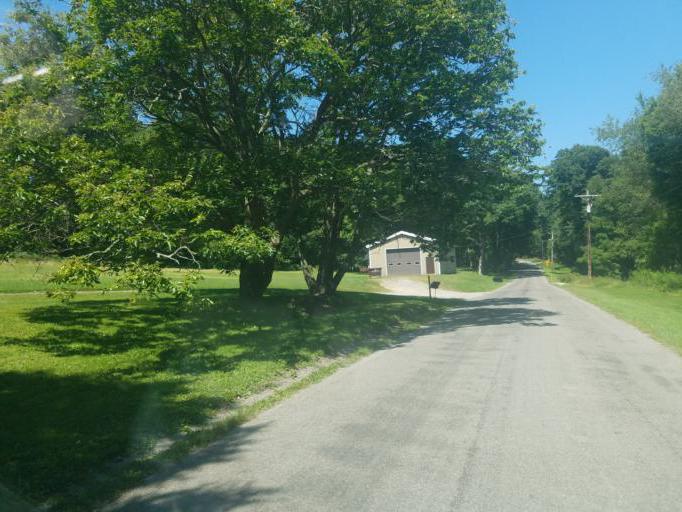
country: US
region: Pennsylvania
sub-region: Clarion County
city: Knox
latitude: 41.1942
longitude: -79.5185
